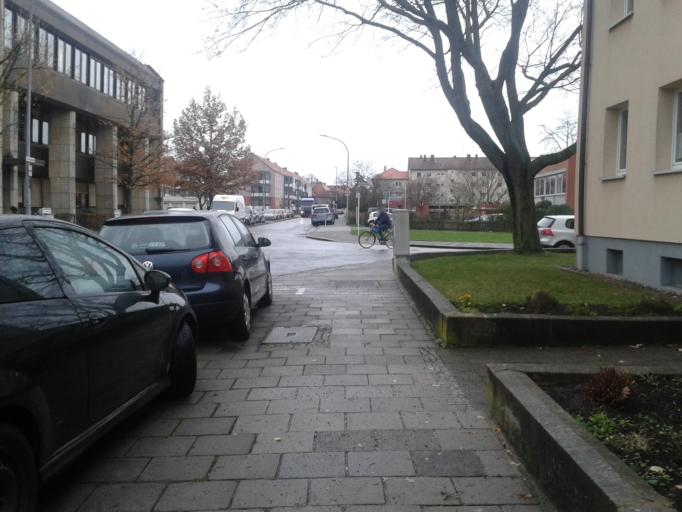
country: DE
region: Bavaria
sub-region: Upper Franconia
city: Bamberg
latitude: 49.9068
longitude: 10.9032
